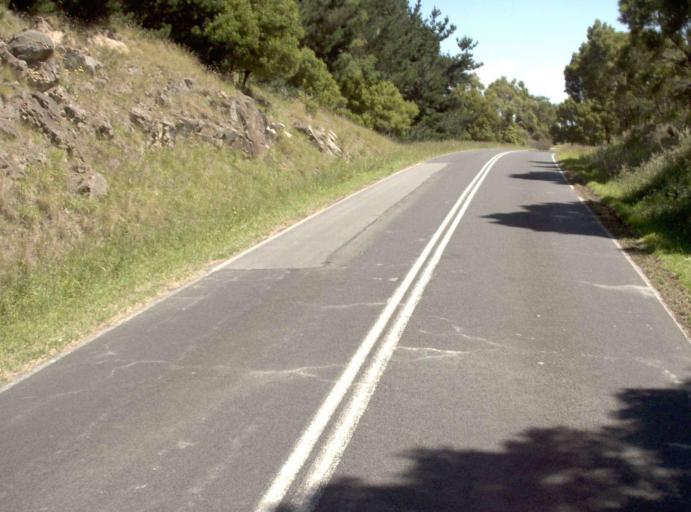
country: AU
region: Victoria
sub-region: Latrobe
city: Morwell
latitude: -38.6718
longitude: 146.1581
